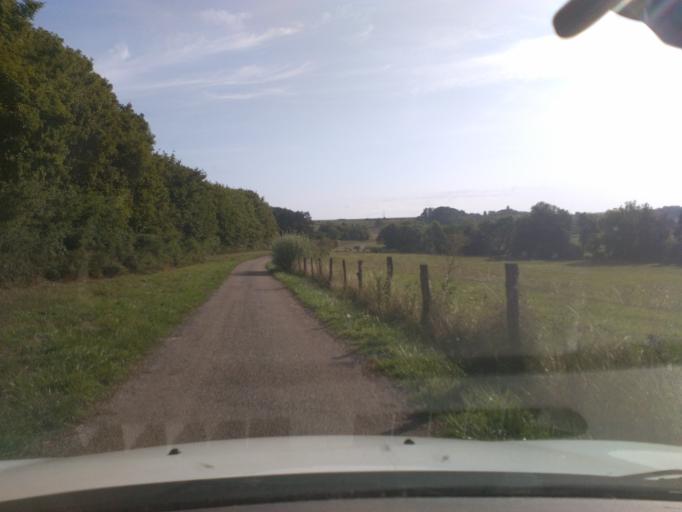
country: FR
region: Lorraine
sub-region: Departement des Vosges
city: Mirecourt
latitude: 48.3105
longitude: 6.0856
